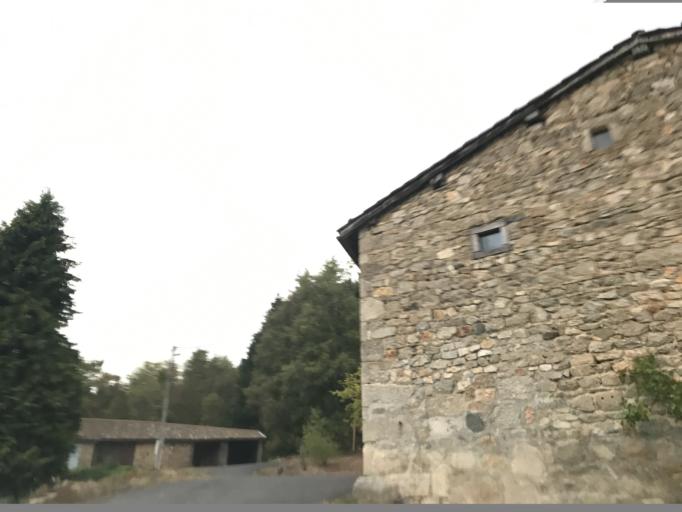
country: FR
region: Auvergne
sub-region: Departement du Puy-de-Dome
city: Thiers
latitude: 45.8372
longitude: 3.5847
